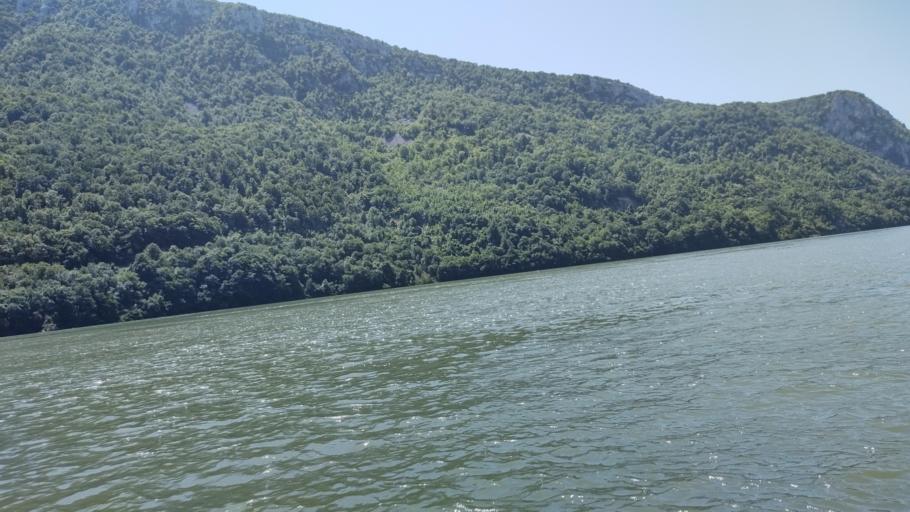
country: RO
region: Mehedinti
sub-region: Comuna Dubova
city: Dubova
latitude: 44.5945
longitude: 22.2619
